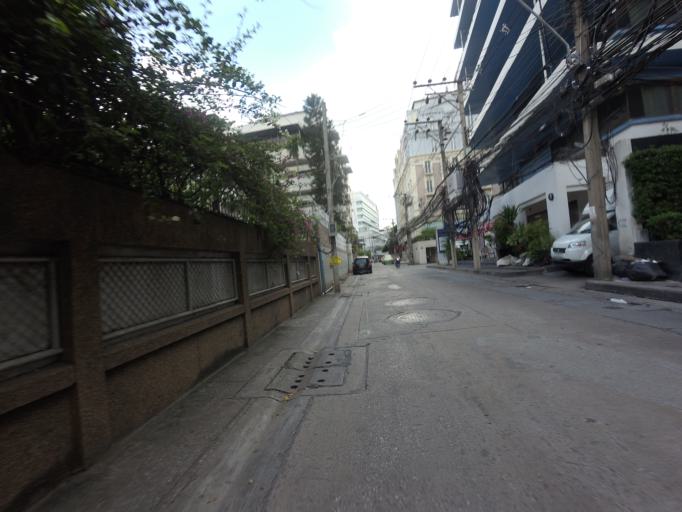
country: TH
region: Bangkok
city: Khlong Toei
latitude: 13.7418
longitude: 100.5586
